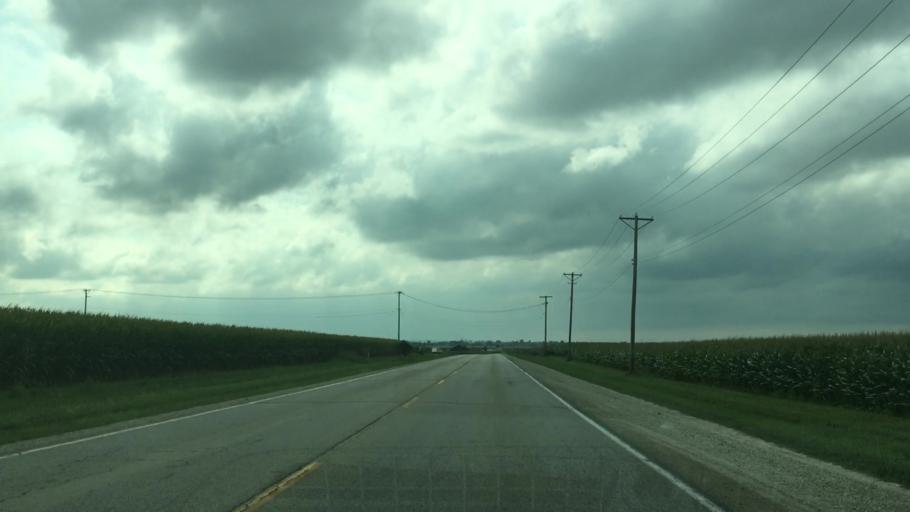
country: US
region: Illinois
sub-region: Ogle County
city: Rochelle
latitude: 41.8978
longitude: -89.0565
